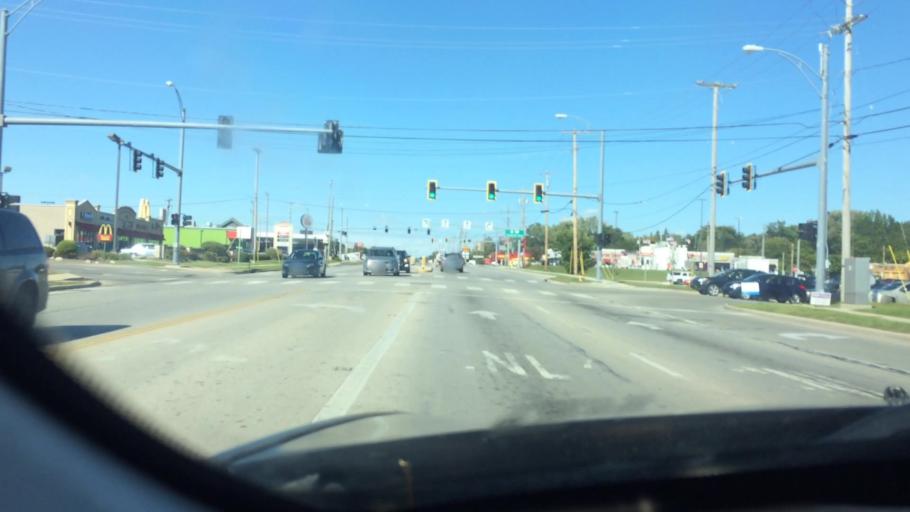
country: US
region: Ohio
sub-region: Lucas County
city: Ottawa Hills
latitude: 41.6744
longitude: -83.6826
